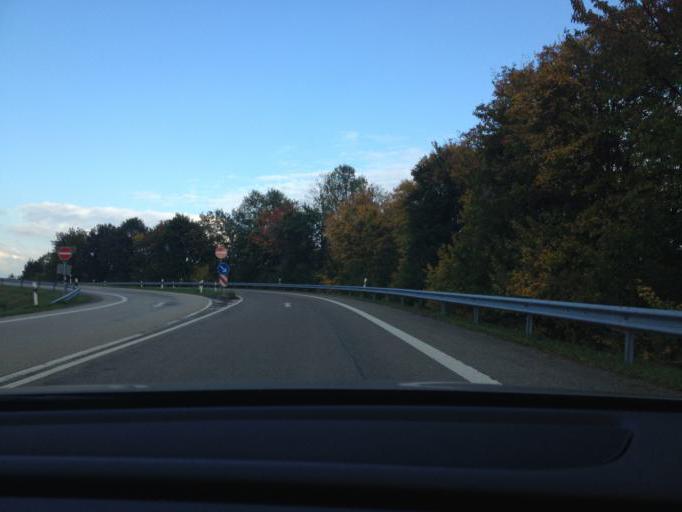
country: DE
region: Rheinland-Pfalz
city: Reichweiler
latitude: 49.5365
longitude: 7.2939
